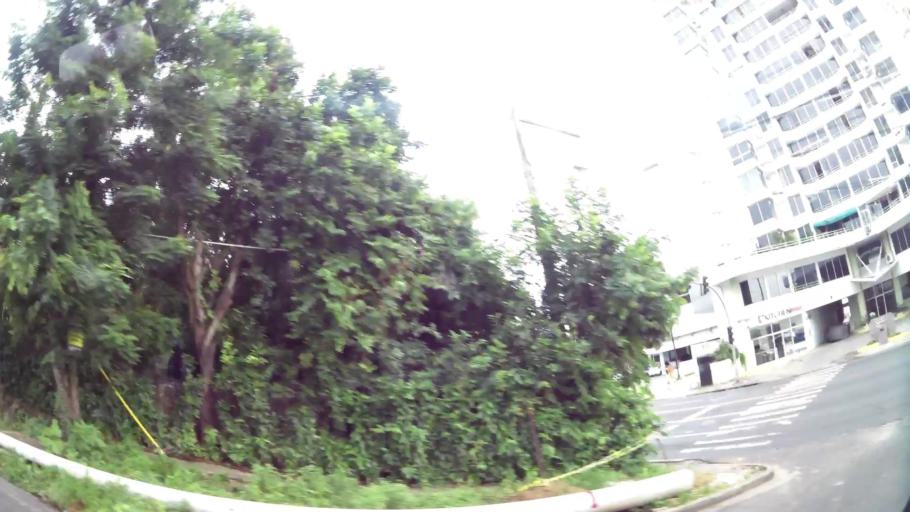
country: PA
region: Panama
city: Panama
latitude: 8.9973
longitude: -79.5057
